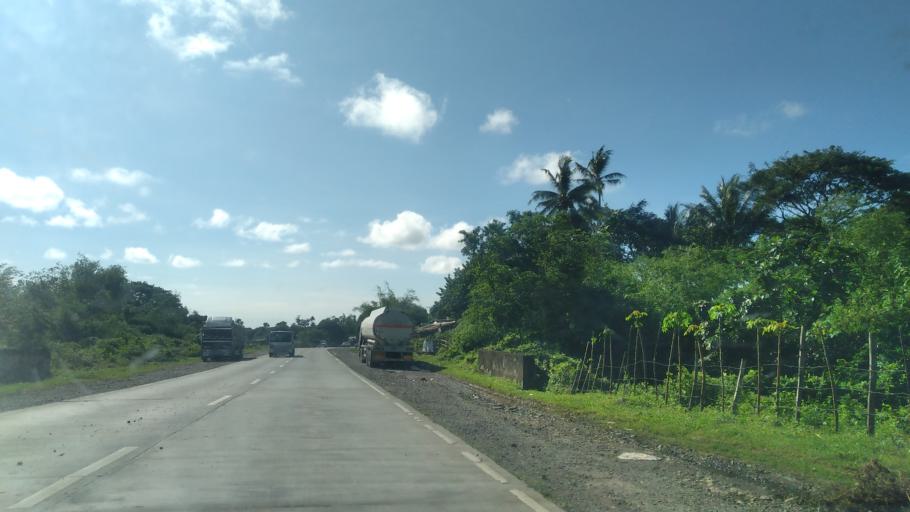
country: PH
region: Calabarzon
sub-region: Province of Quezon
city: Isabang
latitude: 13.9568
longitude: 121.5785
